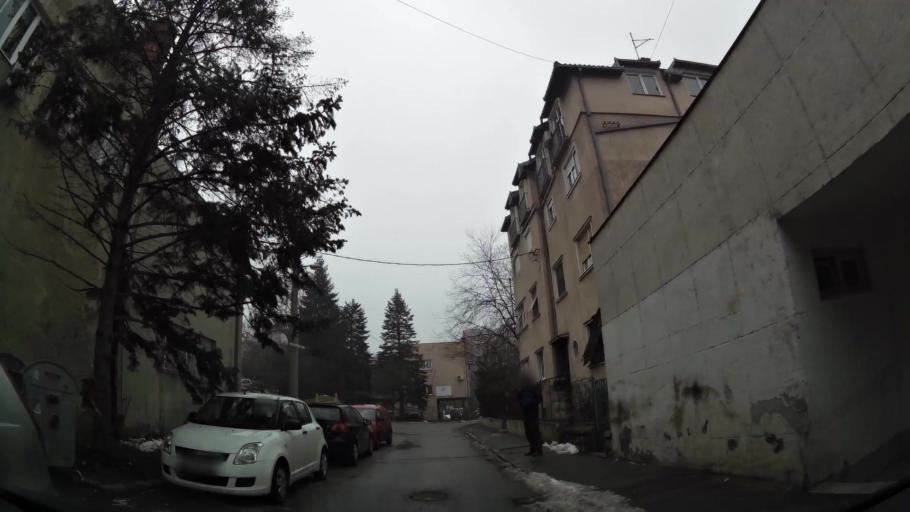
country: RS
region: Central Serbia
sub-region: Belgrade
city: Novi Beograd
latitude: 44.7937
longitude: 20.4347
